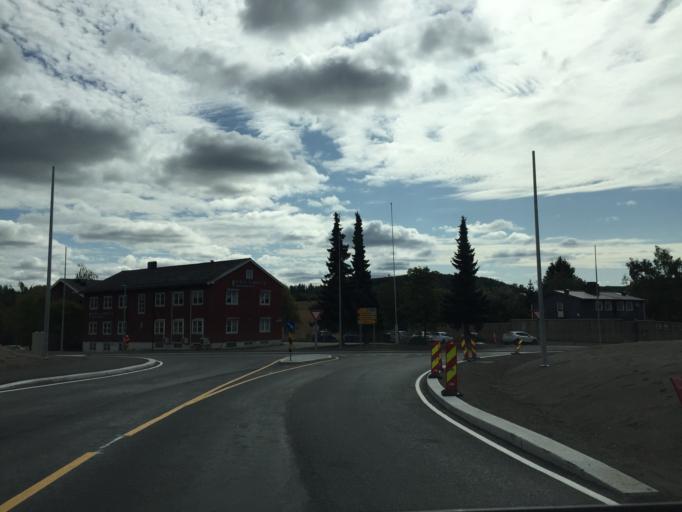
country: NO
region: Ostfold
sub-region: Hobol
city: Elvestad
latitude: 59.6230
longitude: 10.9488
